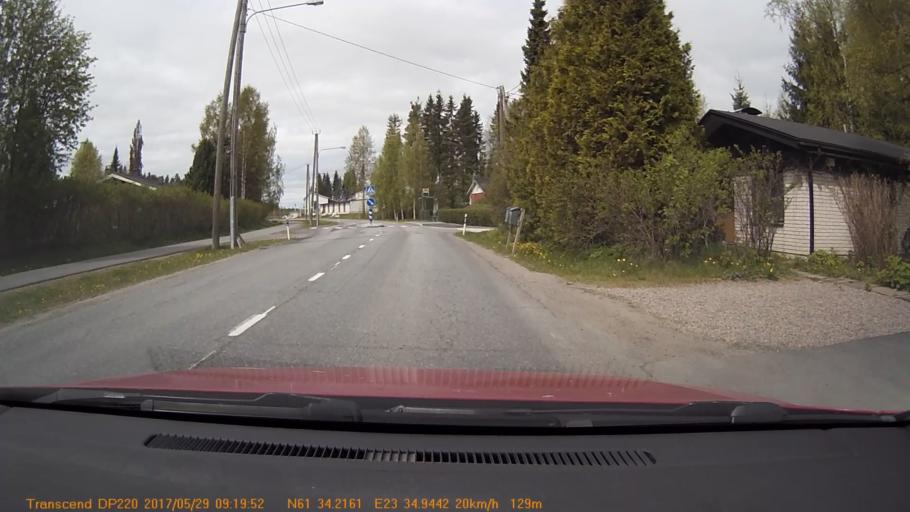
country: FI
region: Pirkanmaa
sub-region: Tampere
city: Yloejaervi
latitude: 61.5702
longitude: 23.5824
